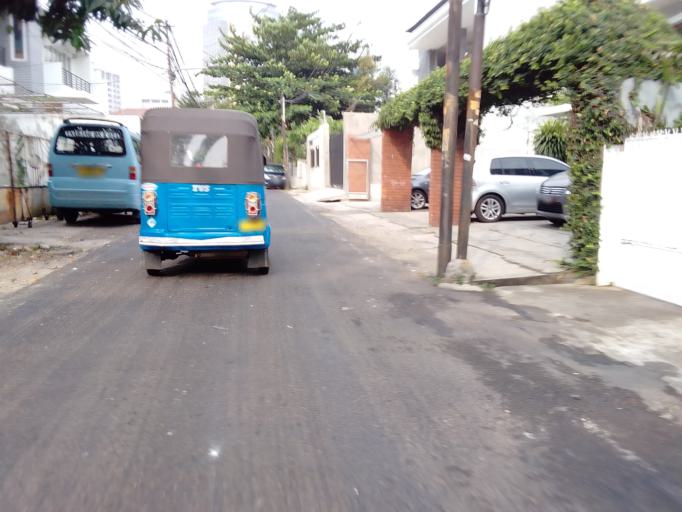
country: ID
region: Jakarta Raya
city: Jakarta
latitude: -6.1794
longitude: 106.8166
